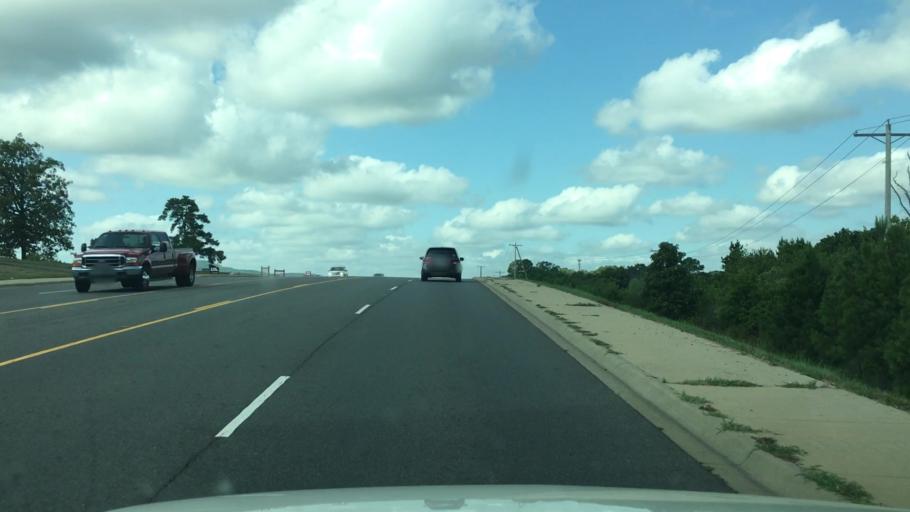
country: US
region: Arkansas
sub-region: Garland County
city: Lake Hamilton
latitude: 34.4526
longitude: -93.0799
